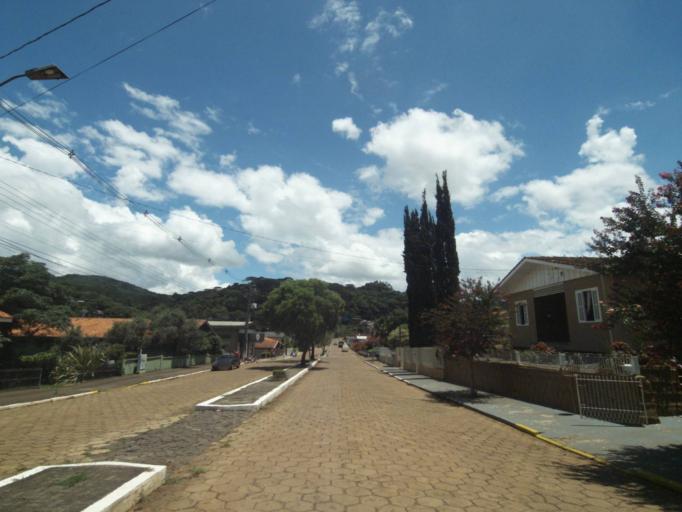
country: BR
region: Parana
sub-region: Uniao Da Vitoria
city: Uniao da Vitoria
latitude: -26.1656
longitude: -51.5555
